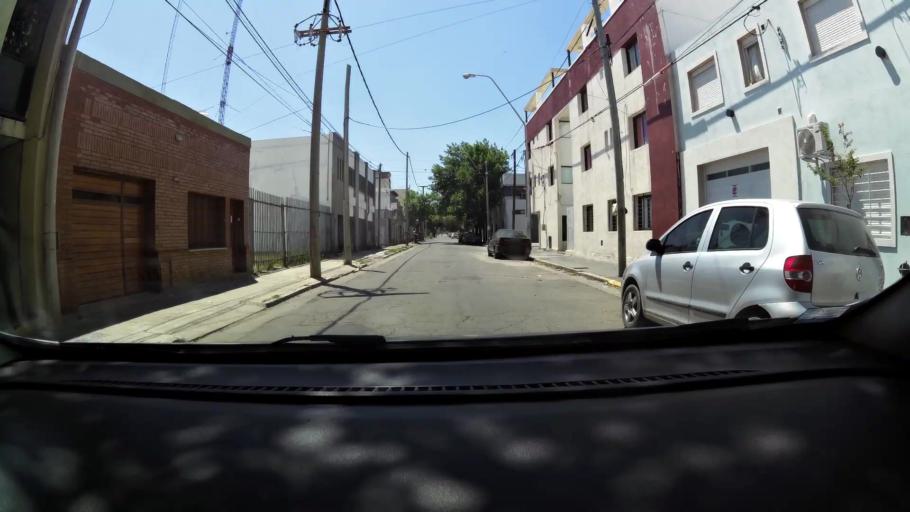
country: AR
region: Cordoba
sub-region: Departamento de Capital
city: Cordoba
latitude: -31.3856
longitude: -64.1999
